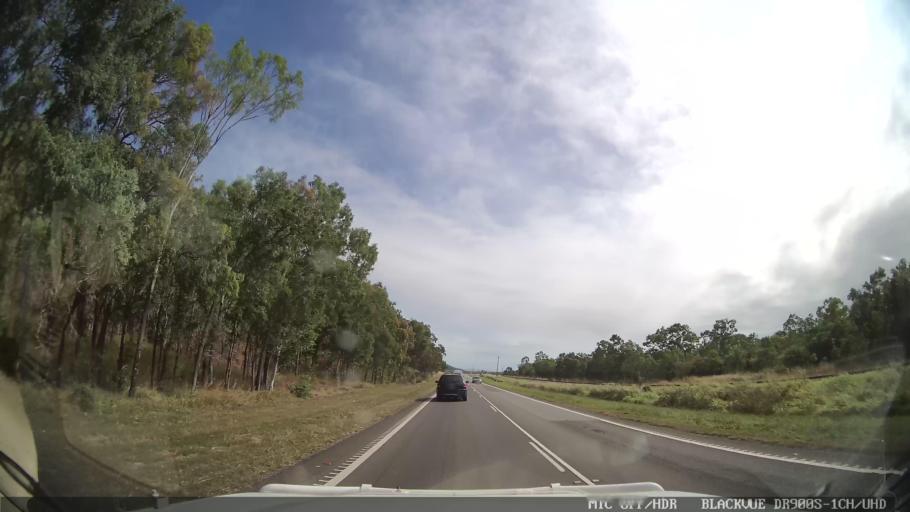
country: AU
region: Queensland
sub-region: Townsville
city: Townsville
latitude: -19.4019
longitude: 147.0257
